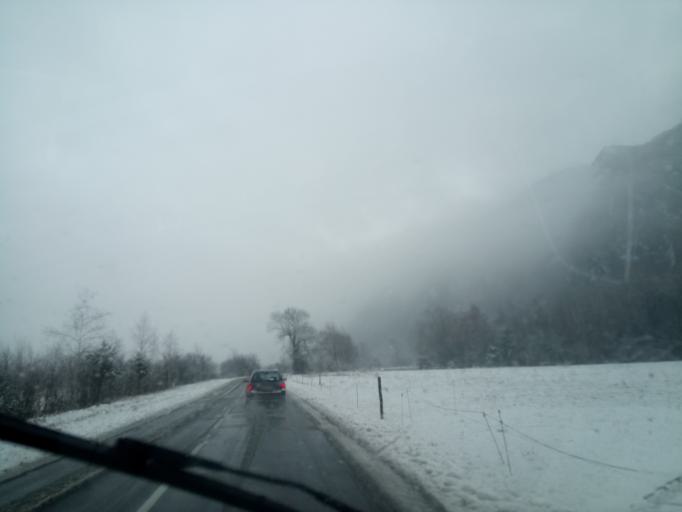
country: FR
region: Rhone-Alpes
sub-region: Departement de la Savoie
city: Saint-Etienne-de-Cuines
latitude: 45.3717
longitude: 6.2767
